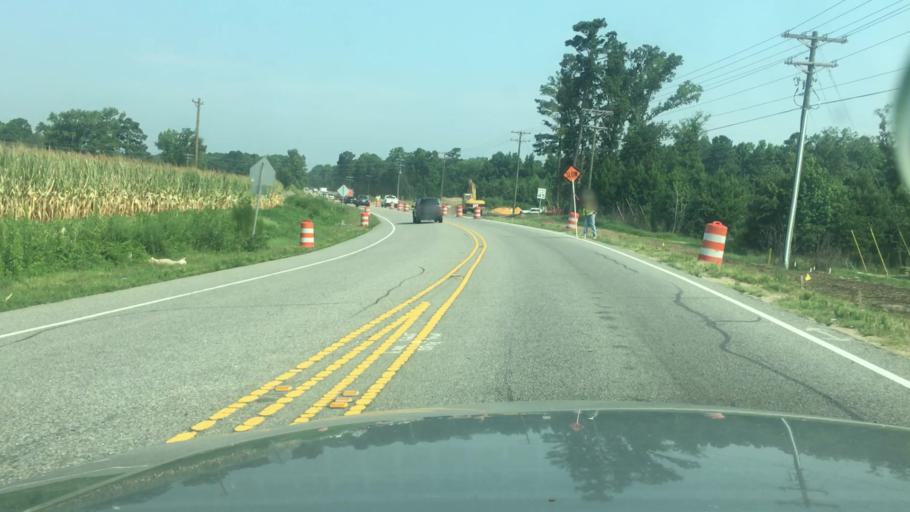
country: US
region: North Carolina
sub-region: Cumberland County
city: Hope Mills
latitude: 34.9265
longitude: -78.9106
